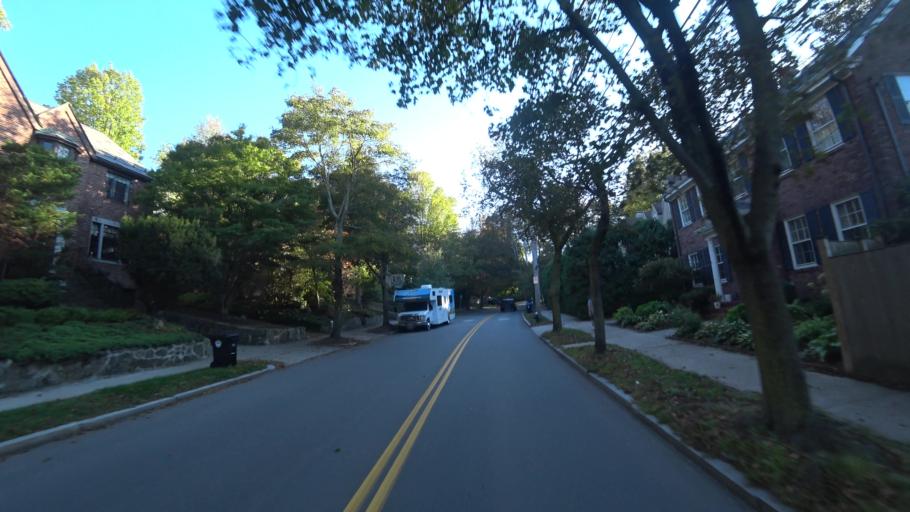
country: US
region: Massachusetts
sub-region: Norfolk County
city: Brookline
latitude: 42.3313
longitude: -71.1316
